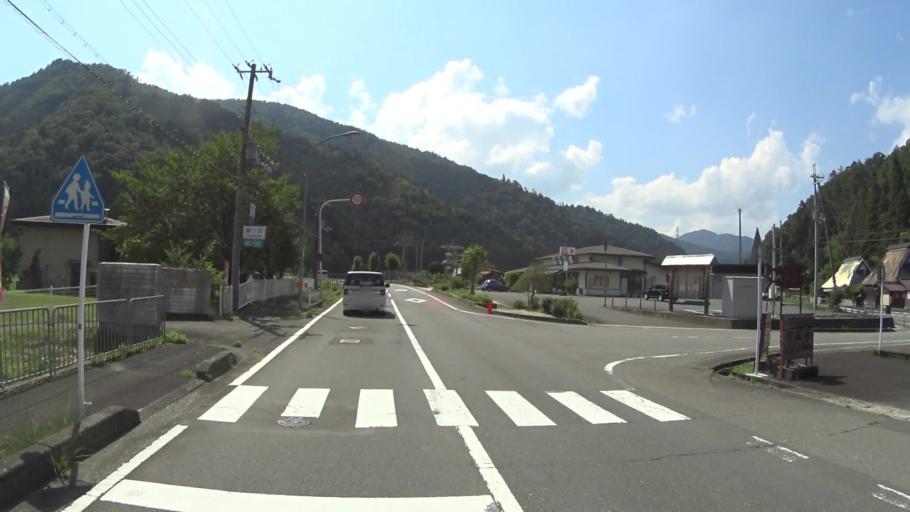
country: JP
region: Fukui
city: Obama
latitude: 35.3218
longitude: 135.5582
